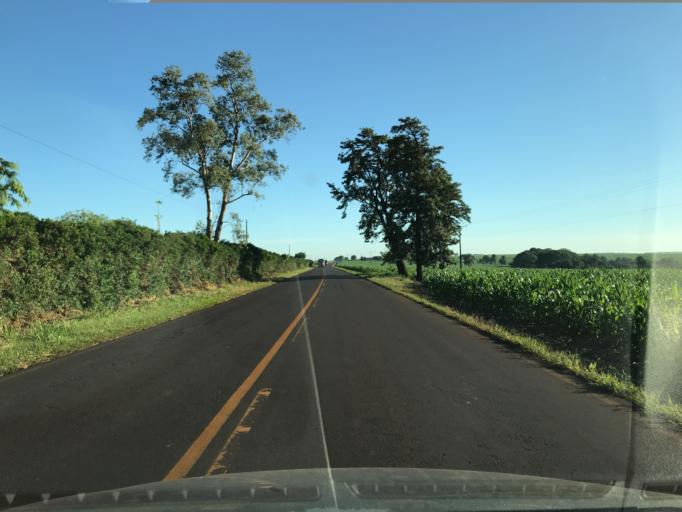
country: BR
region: Parana
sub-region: Palotina
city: Palotina
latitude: -24.1246
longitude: -53.8500
